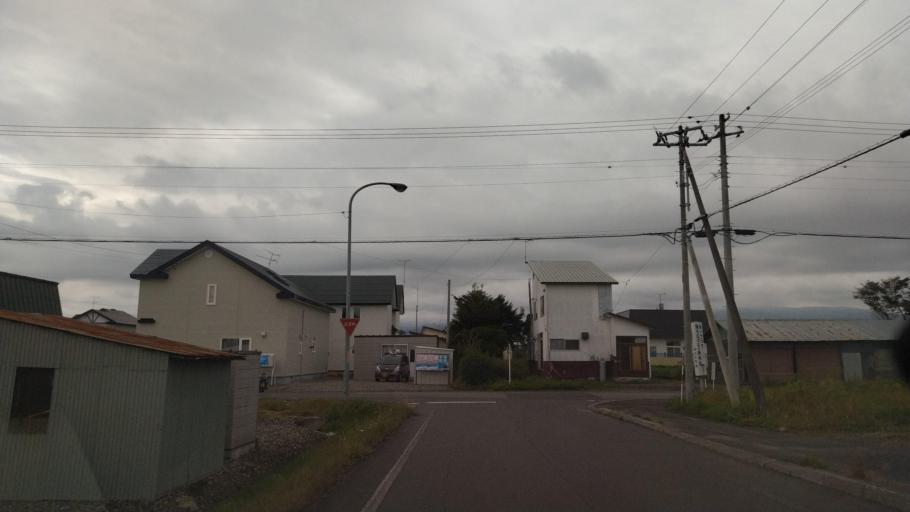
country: JP
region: Hokkaido
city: Otofuke
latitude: 43.2372
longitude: 143.2895
